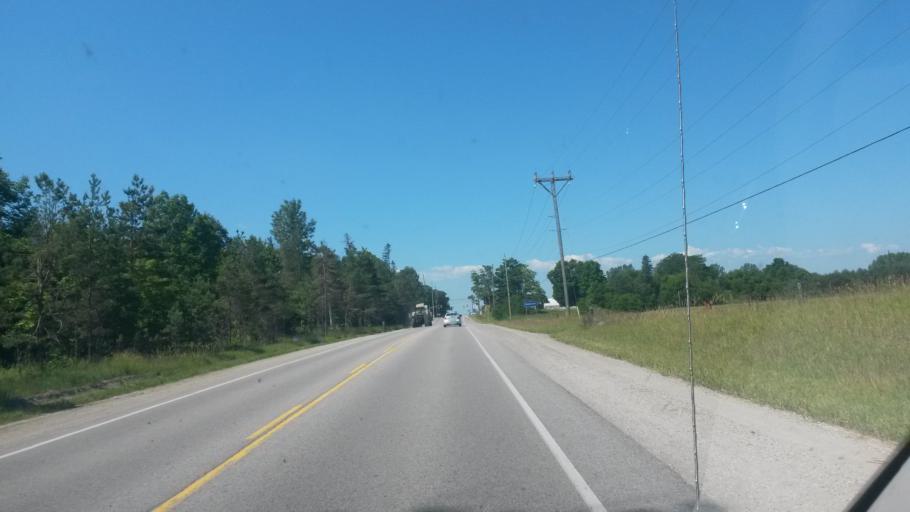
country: CA
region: Ontario
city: Barrie
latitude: 44.5315
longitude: -79.7218
